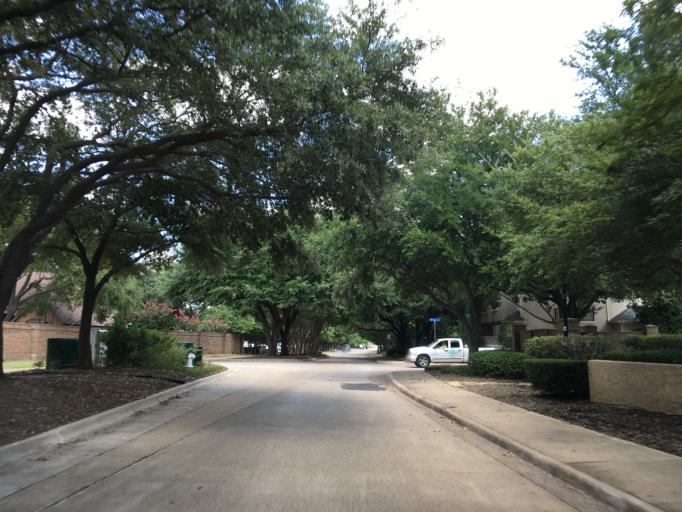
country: US
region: Texas
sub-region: Dallas County
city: Addison
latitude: 32.9459
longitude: -96.8427
